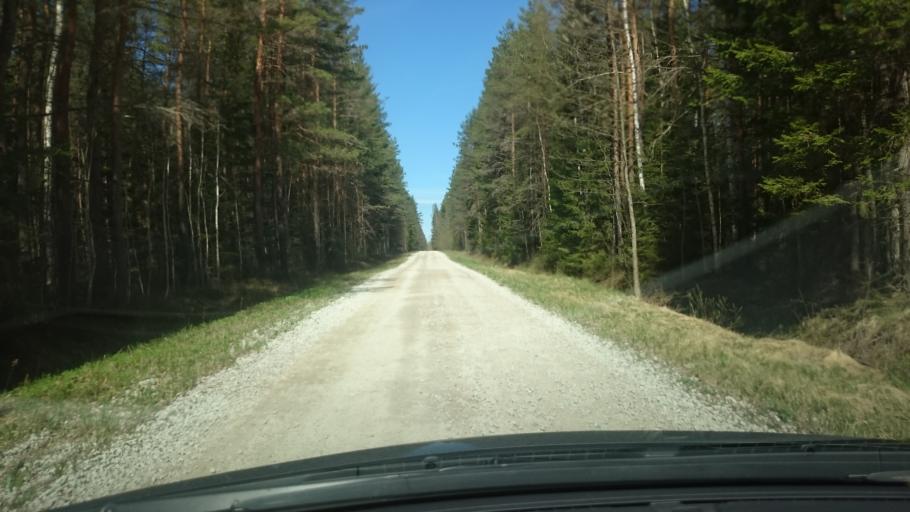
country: EE
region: Ida-Virumaa
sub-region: Sillamaee linn
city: Sillamae
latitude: 59.1588
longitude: 27.8009
